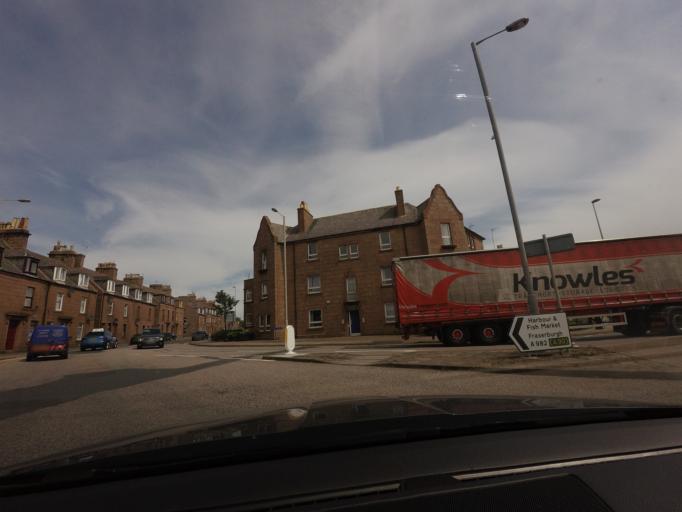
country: GB
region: Scotland
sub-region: Aberdeenshire
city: Peterhead
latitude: 57.5053
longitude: -1.7882
